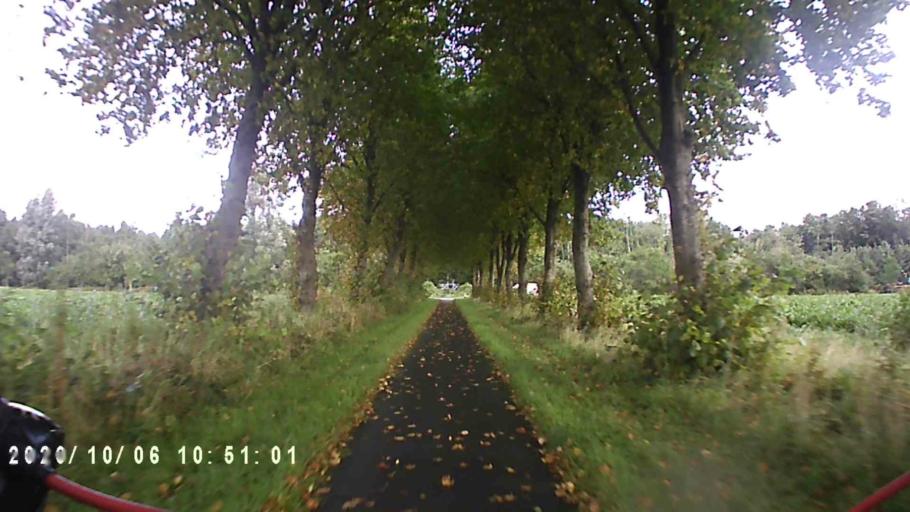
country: NL
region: Groningen
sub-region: Gemeente Zuidhorn
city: Oldehove
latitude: 53.3660
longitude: 6.4110
